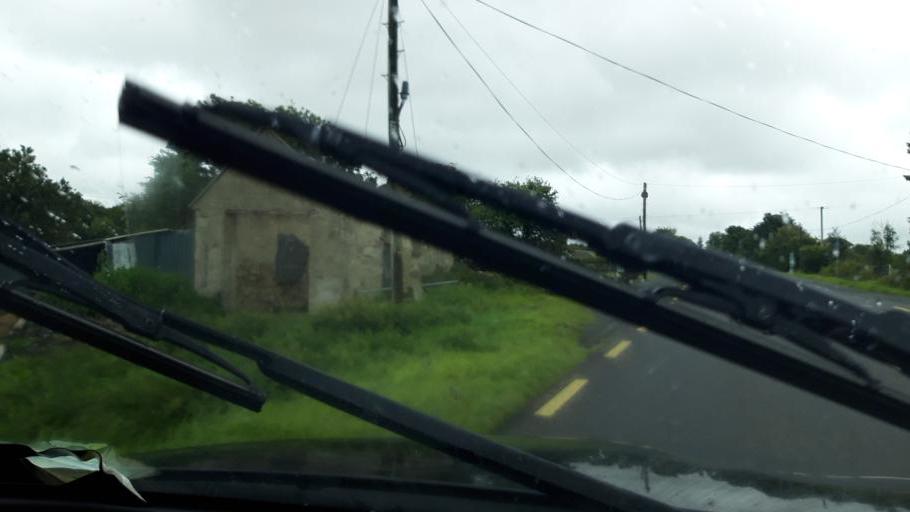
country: IE
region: Leinster
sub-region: Loch Garman
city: New Ross
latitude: 52.4293
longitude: -6.8150
